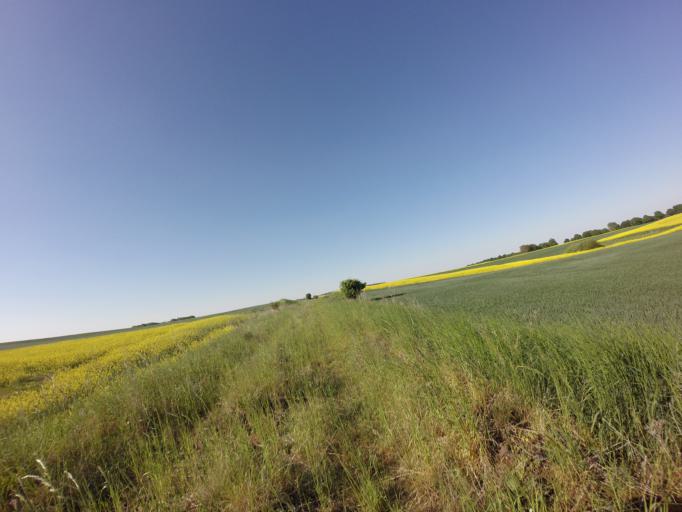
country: PL
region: West Pomeranian Voivodeship
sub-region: Powiat choszczenski
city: Choszczno
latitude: 53.1457
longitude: 15.3712
